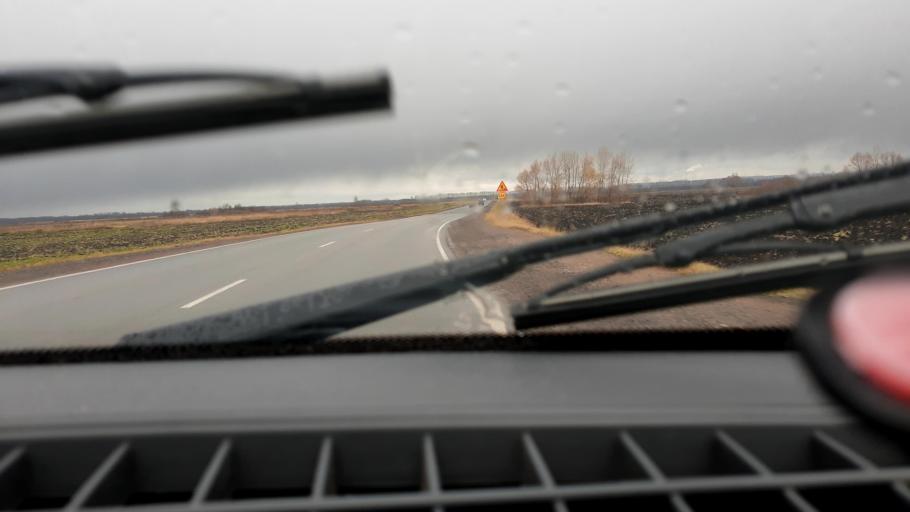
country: RU
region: Bashkortostan
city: Ufa
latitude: 54.8038
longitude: 55.9639
